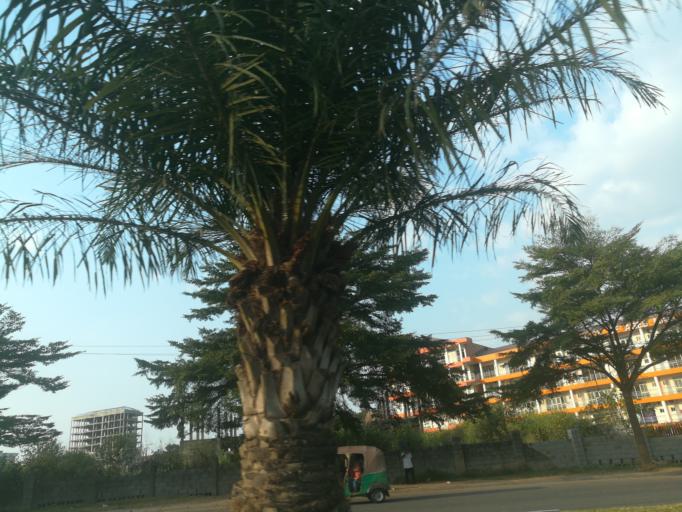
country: NG
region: Abuja Federal Capital Territory
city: Abuja
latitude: 9.0665
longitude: 7.4346
